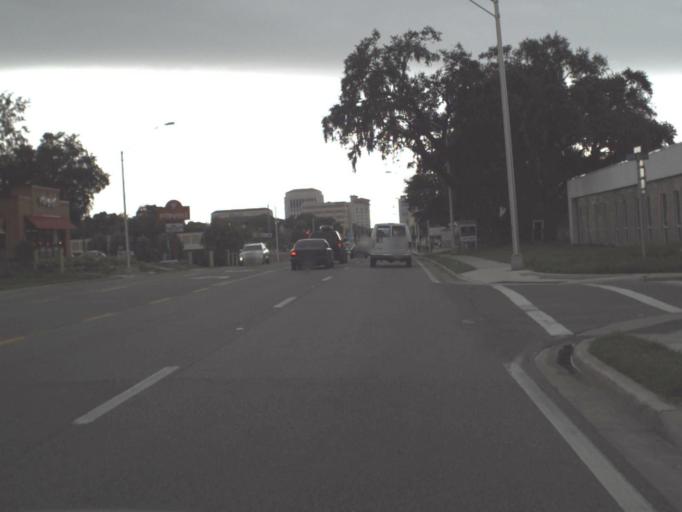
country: US
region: Florida
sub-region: Sarasota County
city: Sarasota
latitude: 27.3440
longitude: -82.5311
